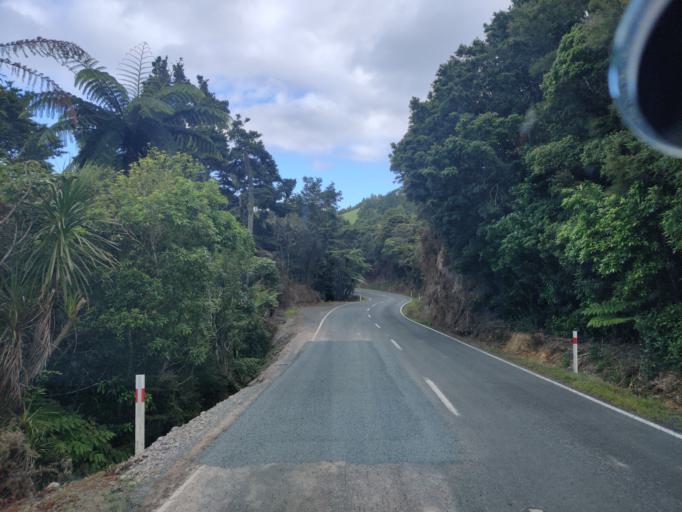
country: NZ
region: Northland
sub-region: Whangarei
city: Ngunguru
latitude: -35.5820
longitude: 174.4236
